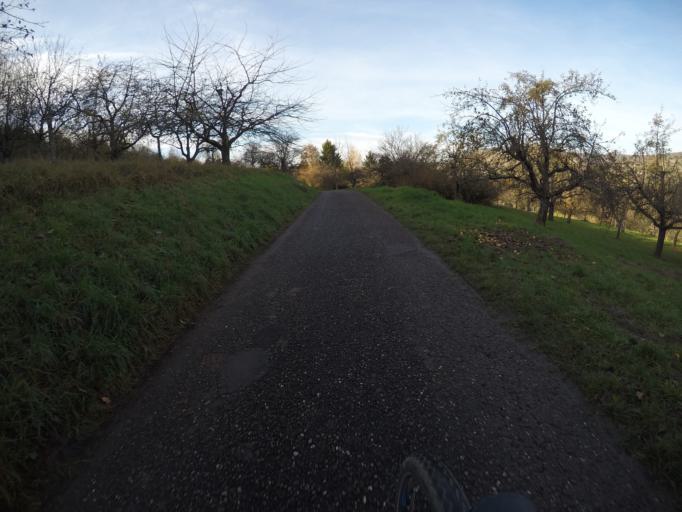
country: DE
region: Baden-Wuerttemberg
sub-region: Regierungsbezirk Stuttgart
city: Weinstadt-Endersbach
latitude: 48.8070
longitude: 9.4043
